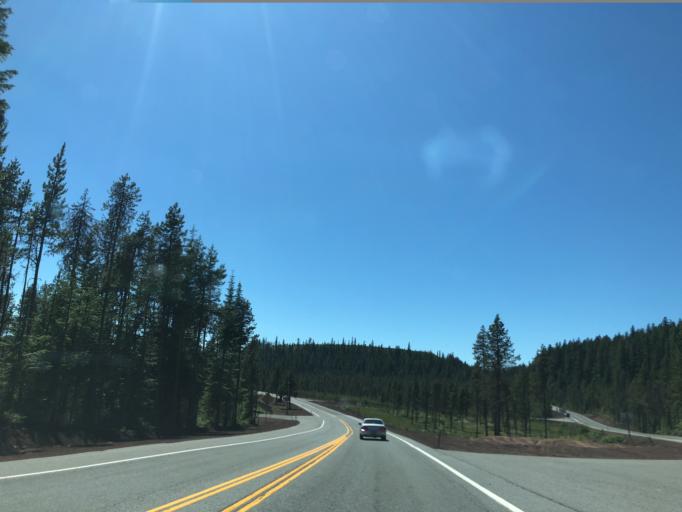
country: US
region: Oregon
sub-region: Deschutes County
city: Sisters
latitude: 44.4366
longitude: -121.9395
